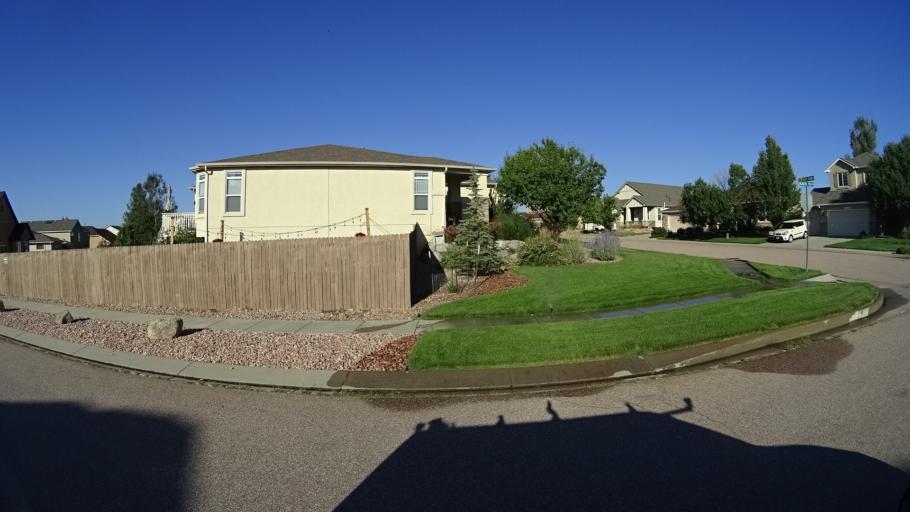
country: US
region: Colorado
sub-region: El Paso County
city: Black Forest
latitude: 38.9853
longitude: -104.7708
